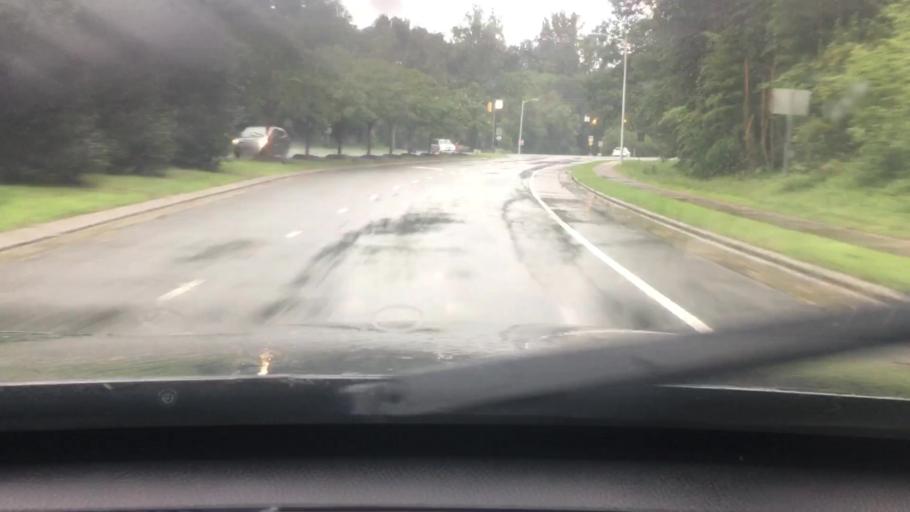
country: US
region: North Carolina
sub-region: Alamance County
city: Glen Raven
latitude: 36.0900
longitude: -79.4668
